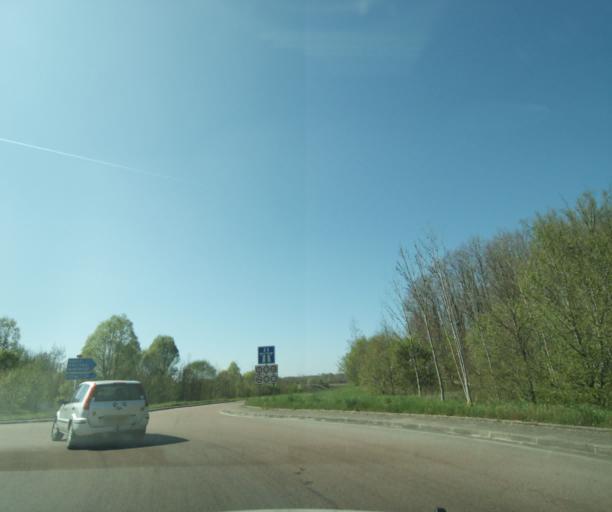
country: FR
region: Bourgogne
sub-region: Departement de la Nievre
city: Pouilly-sur-Loire
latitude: 47.3413
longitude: 2.9303
